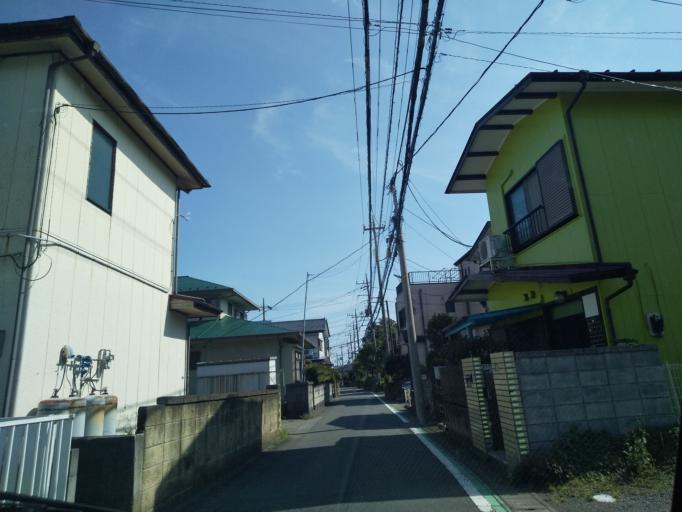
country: JP
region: Kanagawa
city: Minami-rinkan
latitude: 35.4637
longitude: 139.4180
